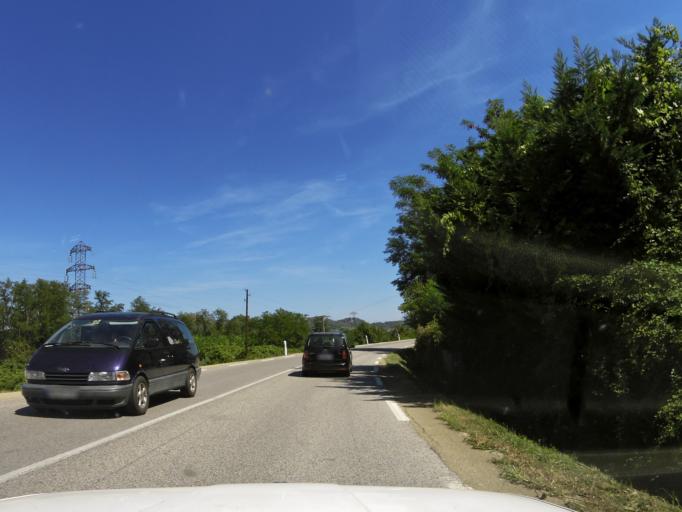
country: FR
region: Languedoc-Roussillon
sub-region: Departement du Gard
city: Sabran
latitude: 44.1678
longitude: 4.5732
